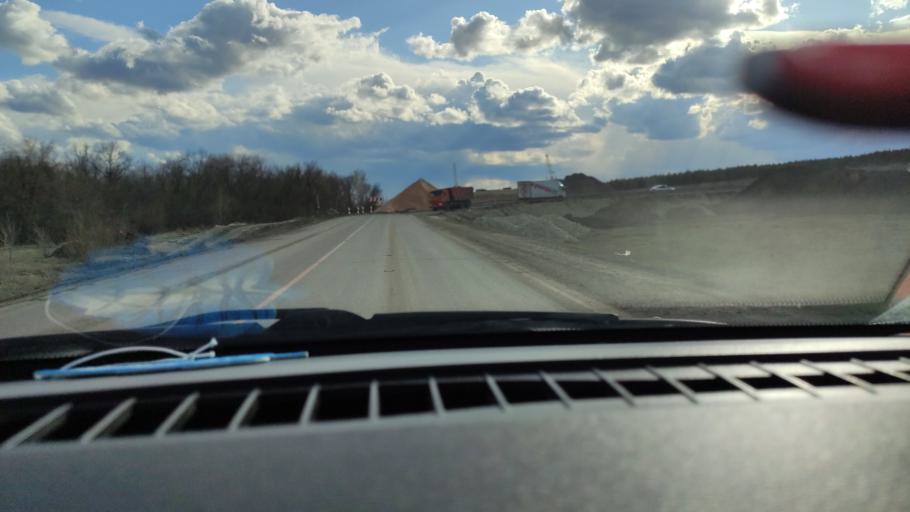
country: RU
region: Saratov
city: Sinodskoye
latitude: 52.0145
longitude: 46.6927
